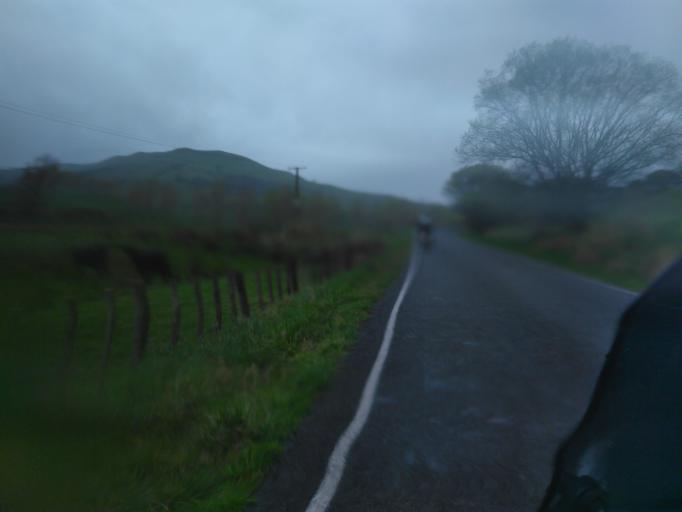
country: NZ
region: Gisborne
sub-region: Gisborne District
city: Gisborne
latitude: -38.6767
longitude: 177.7220
